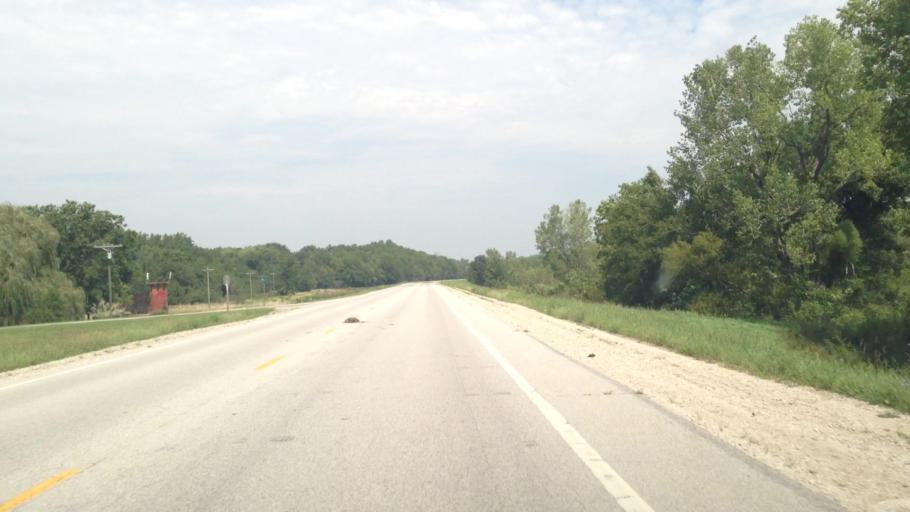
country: US
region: Kansas
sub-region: Neosho County
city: Erie
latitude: 37.5358
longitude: -95.2701
